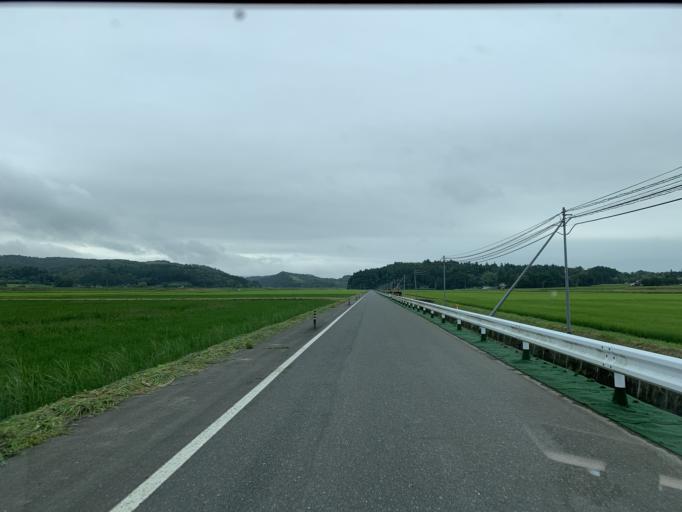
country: JP
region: Iwate
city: Ichinoseki
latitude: 38.8156
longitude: 141.2014
